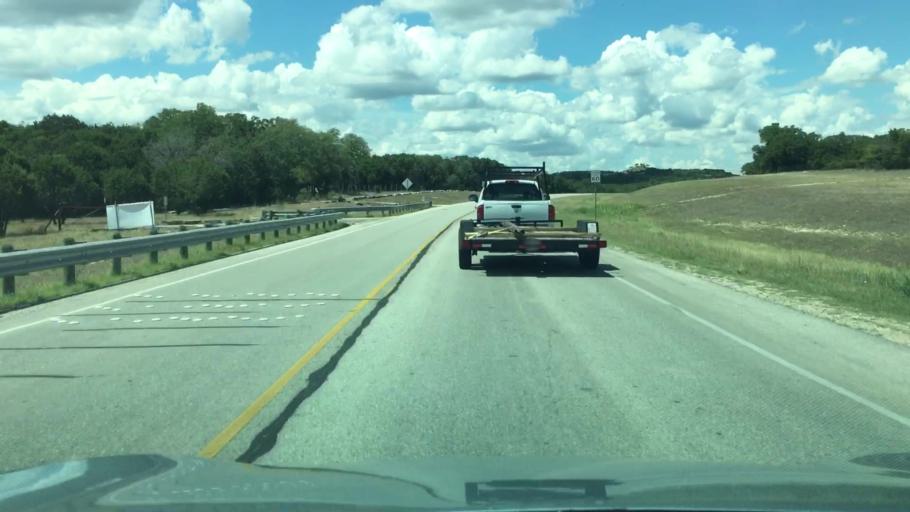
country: US
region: Texas
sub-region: Hays County
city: Wimberley
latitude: 30.0075
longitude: -98.0815
